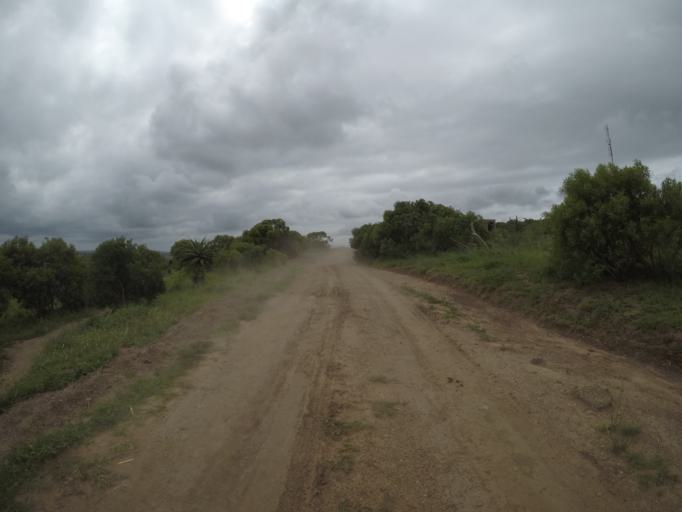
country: ZA
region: KwaZulu-Natal
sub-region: uThungulu District Municipality
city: Empangeni
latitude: -28.6042
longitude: 31.8333
